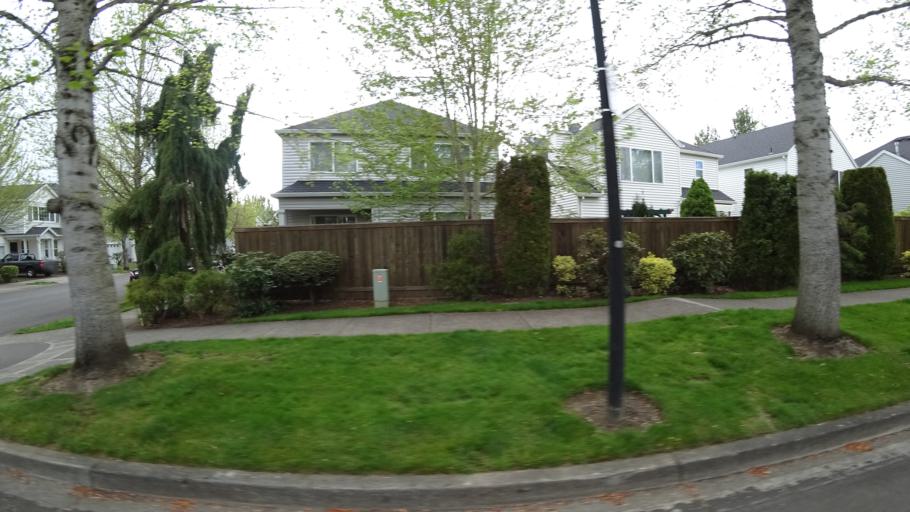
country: US
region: Oregon
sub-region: Washington County
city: Hillsboro
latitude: 45.5452
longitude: -122.9695
